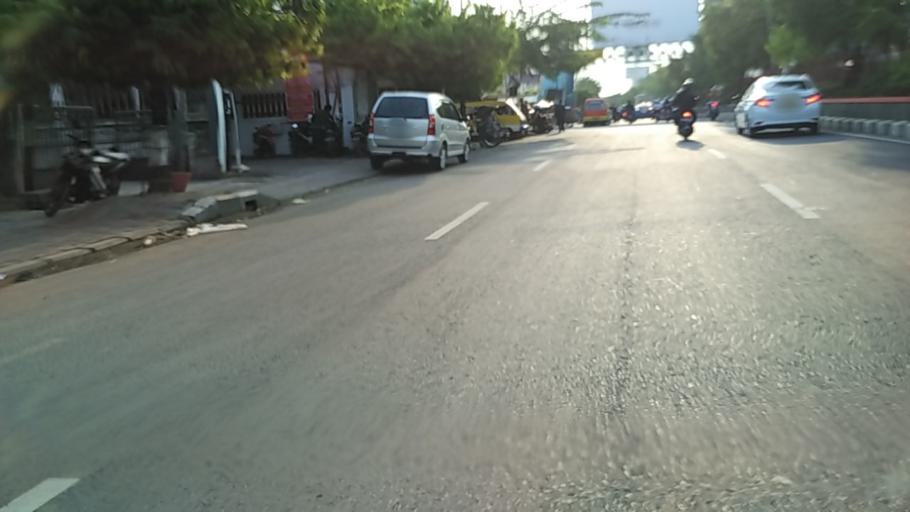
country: ID
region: Central Java
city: Semarang
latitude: -6.9816
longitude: 110.3958
